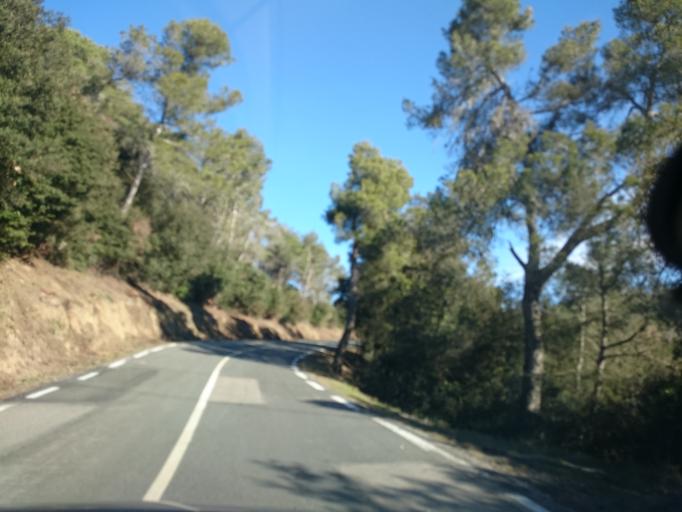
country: ES
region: Catalonia
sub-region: Provincia de Barcelona
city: Molins de Rei
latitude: 41.4279
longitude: 2.0474
